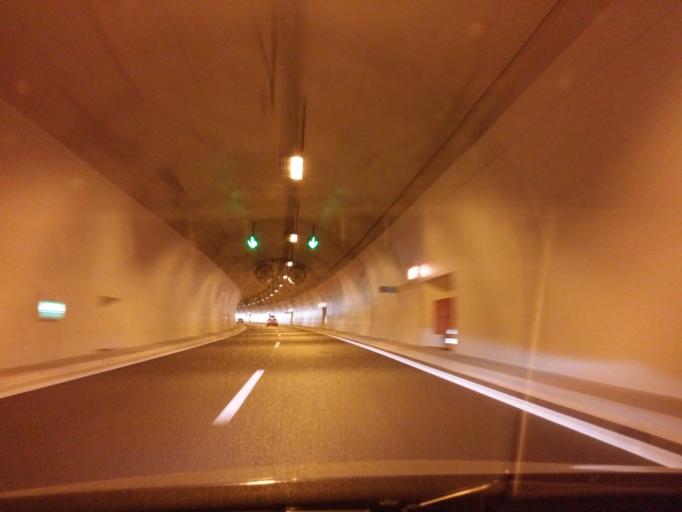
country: GR
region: Peloponnese
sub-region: Nomos Korinthias
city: Nemea
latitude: 37.6917
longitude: 22.5241
